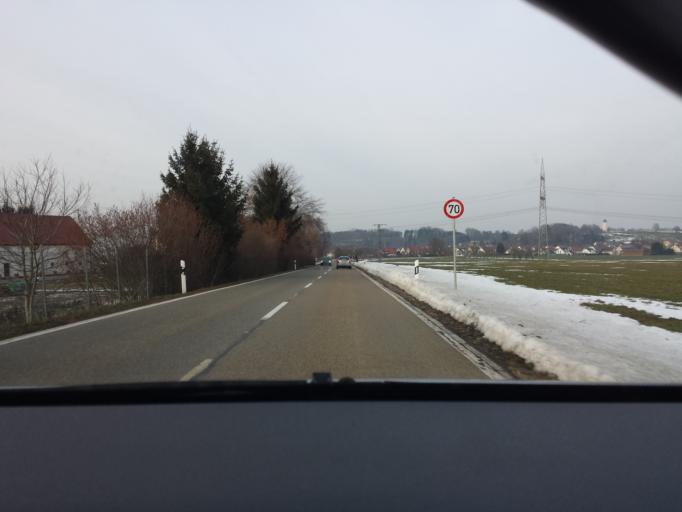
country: DE
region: Baden-Wuerttemberg
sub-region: Tuebingen Region
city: Huttisheim
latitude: 48.2714
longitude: 9.9372
